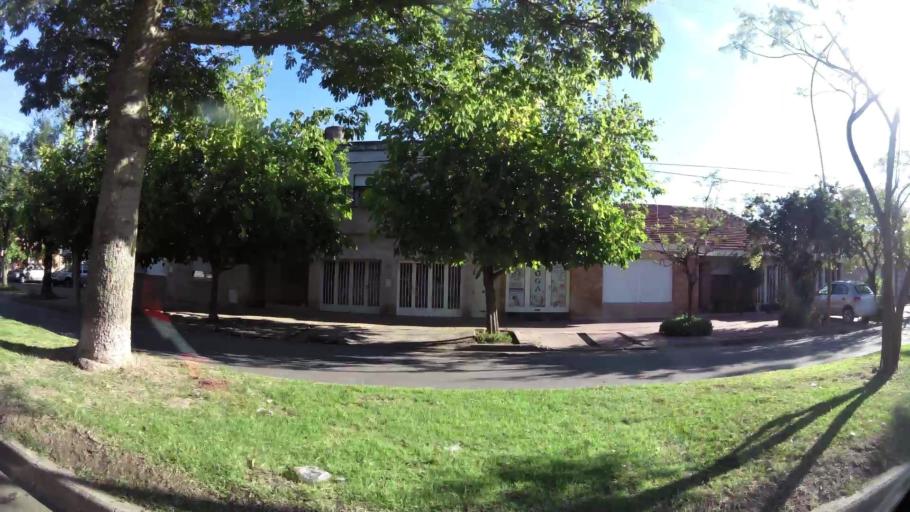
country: AR
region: Cordoba
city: San Francisco
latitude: -31.4367
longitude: -62.0789
